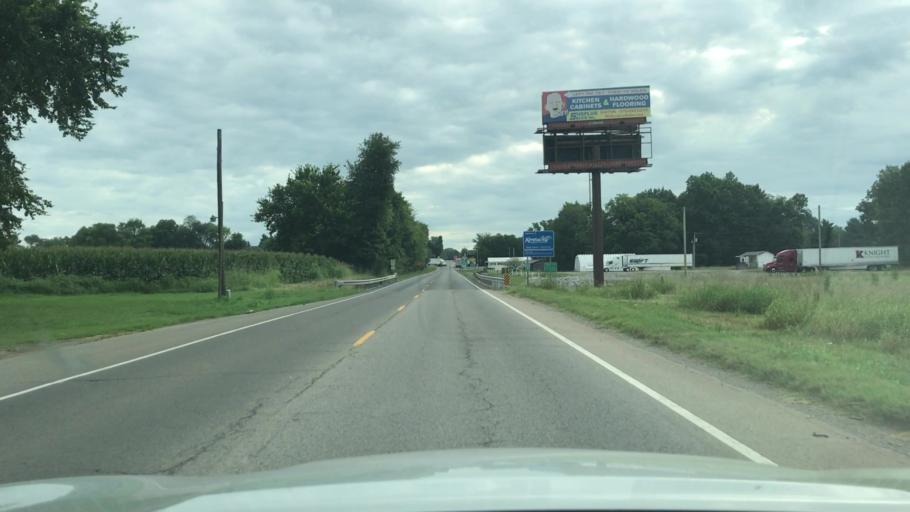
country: US
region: Kentucky
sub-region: Todd County
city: Guthrie
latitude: 36.6415
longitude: -87.2041
